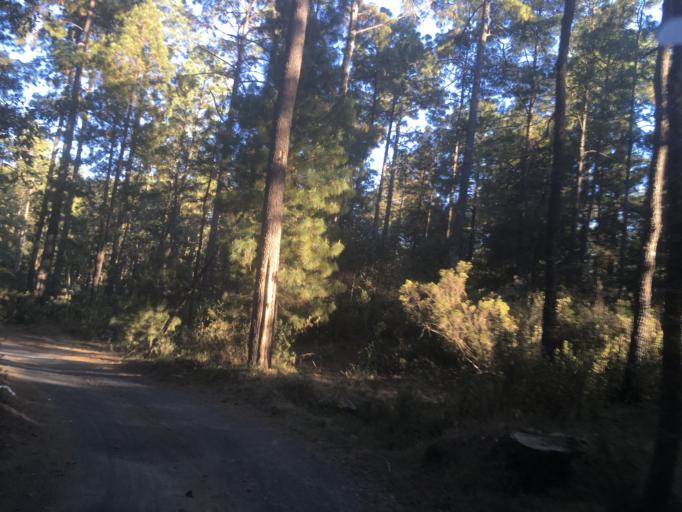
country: MX
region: Michoacan
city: Angahuan
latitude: 19.4602
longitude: -102.2118
